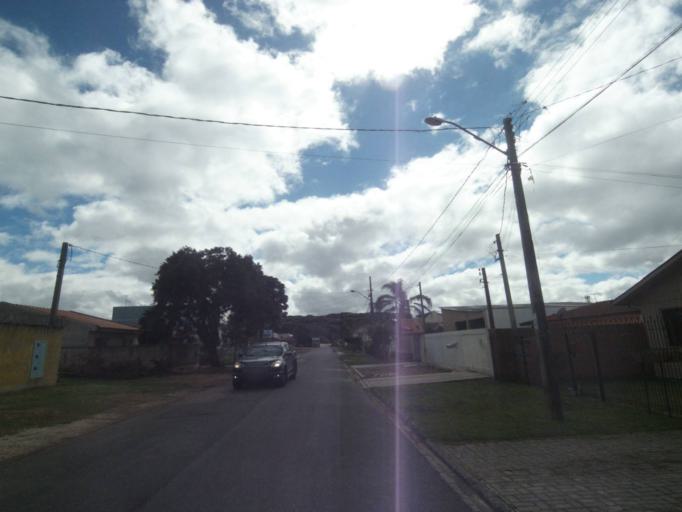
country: BR
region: Parana
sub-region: Sao Jose Dos Pinhais
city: Sao Jose dos Pinhais
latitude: -25.5385
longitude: -49.2907
